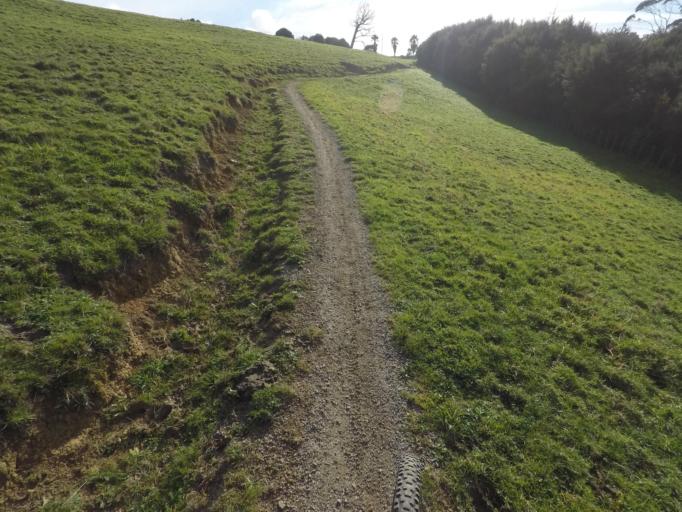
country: NZ
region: Auckland
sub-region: Auckland
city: Manukau City
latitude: -36.9903
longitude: 174.9120
